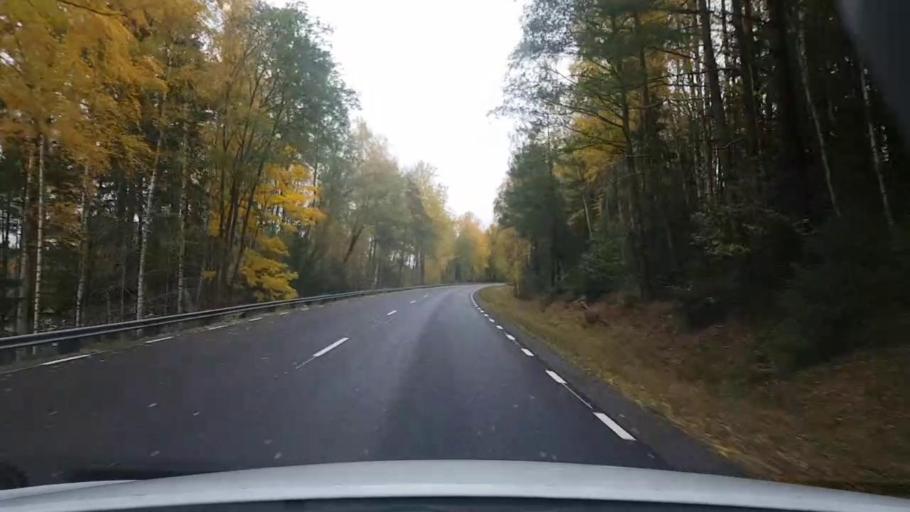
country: SE
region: OErebro
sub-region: Laxa Kommun
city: Laxa
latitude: 58.8232
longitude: 14.5471
